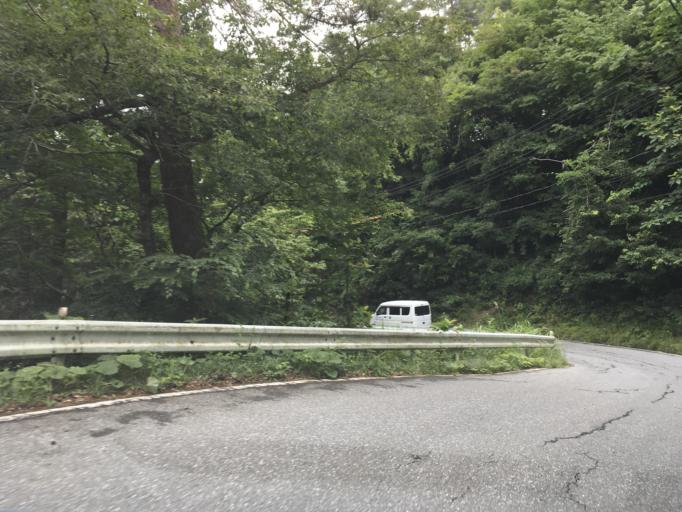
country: JP
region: Iwate
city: Ofunato
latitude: 38.9164
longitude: 141.6056
